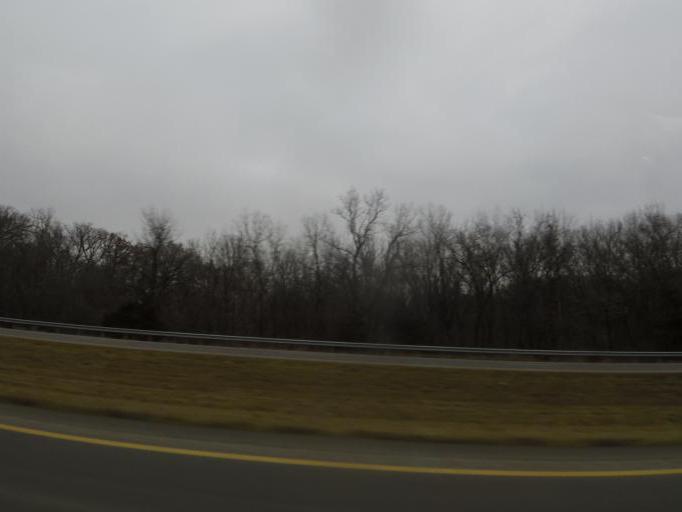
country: US
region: Missouri
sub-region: Marion County
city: Hannibal
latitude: 39.7366
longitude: -91.4109
